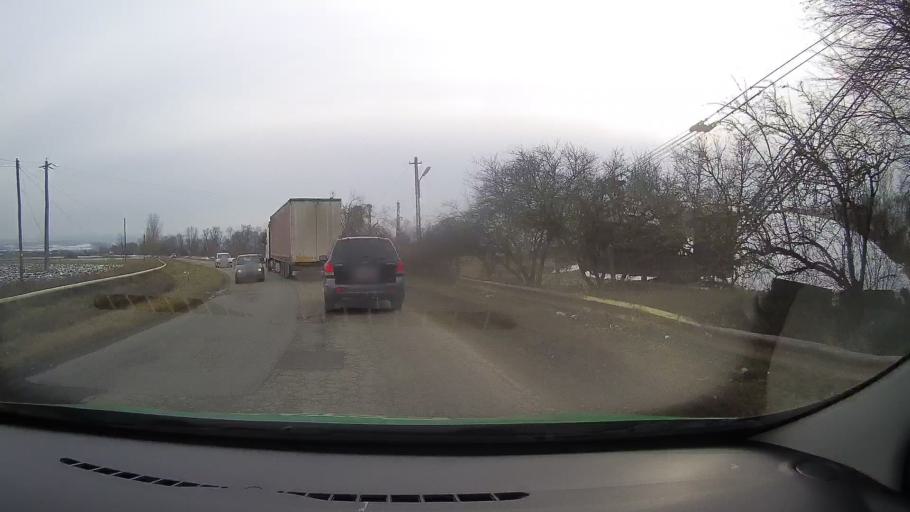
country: RO
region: Hunedoara
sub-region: Comuna Geoagiu
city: Geoagiu
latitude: 45.8947
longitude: 23.2263
